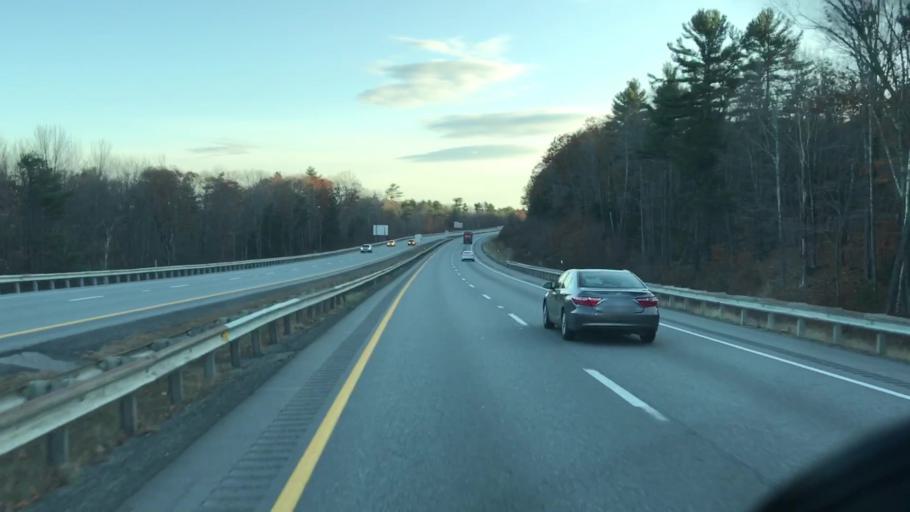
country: US
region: Maine
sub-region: Cumberland County
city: Cumberland Center
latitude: 43.8588
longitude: -70.3238
